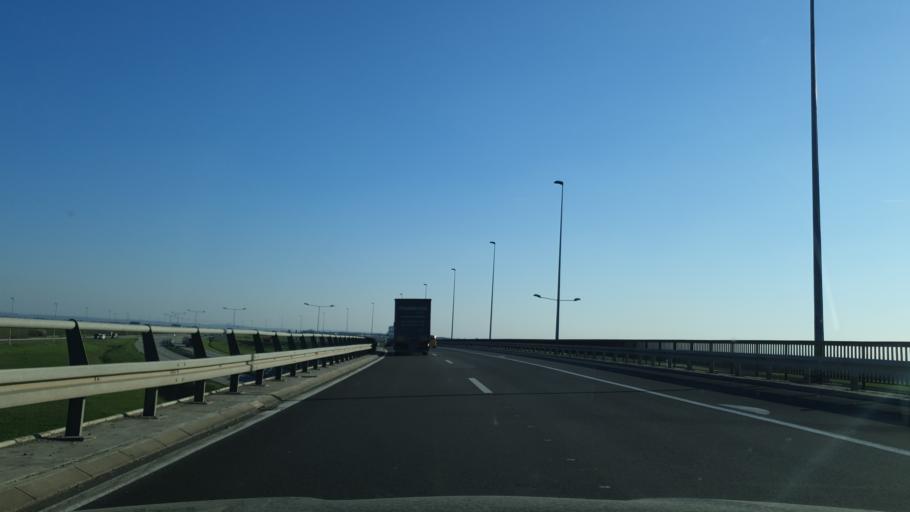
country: RS
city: Dobanovci
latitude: 44.8307
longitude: 20.2504
